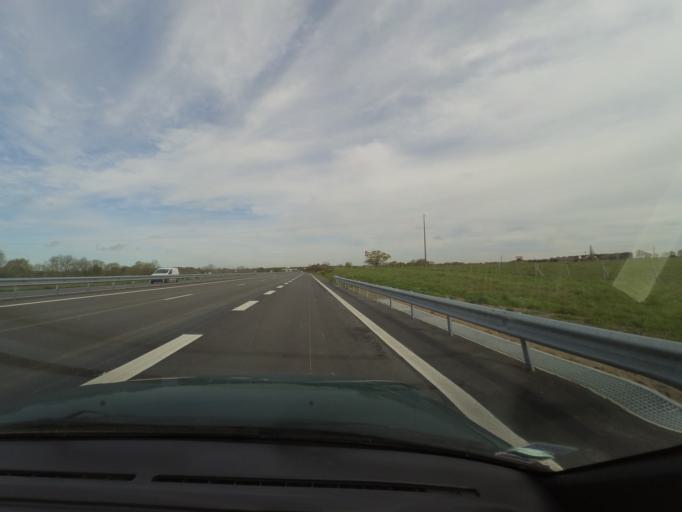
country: FR
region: Pays de la Loire
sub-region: Departement de la Loire-Atlantique
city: Aigrefeuille-sur-Maine
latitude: 47.0731
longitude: -1.4381
